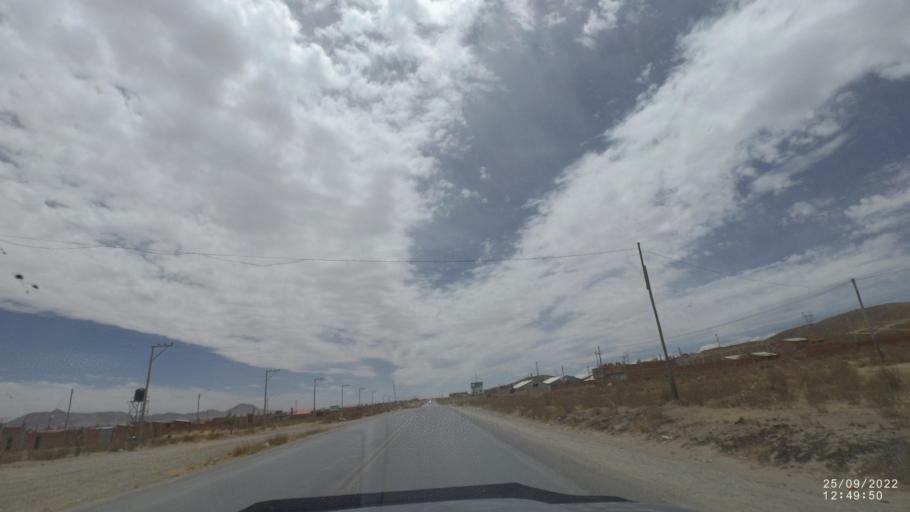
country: BO
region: Oruro
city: Oruro
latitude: -18.0054
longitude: -67.0404
